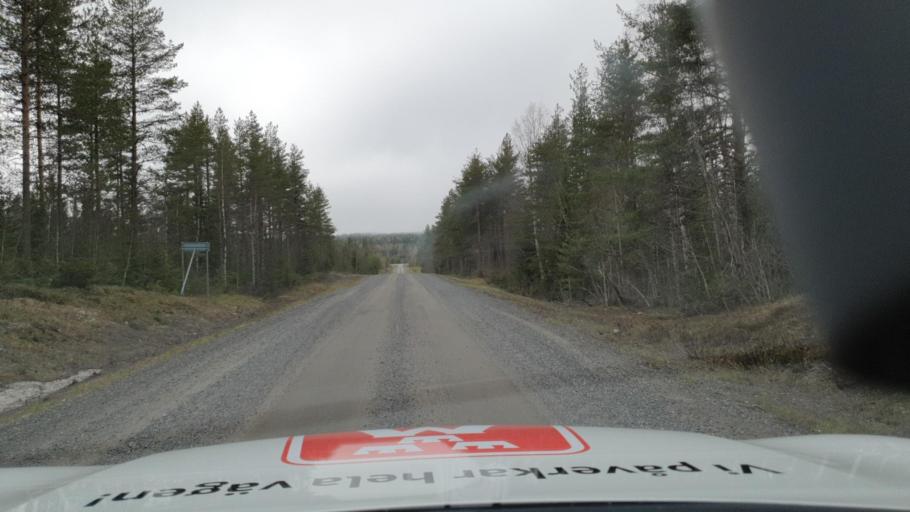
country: SE
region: Vaesterbotten
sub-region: Bjurholms Kommun
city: Bjurholm
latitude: 63.7913
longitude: 19.3182
